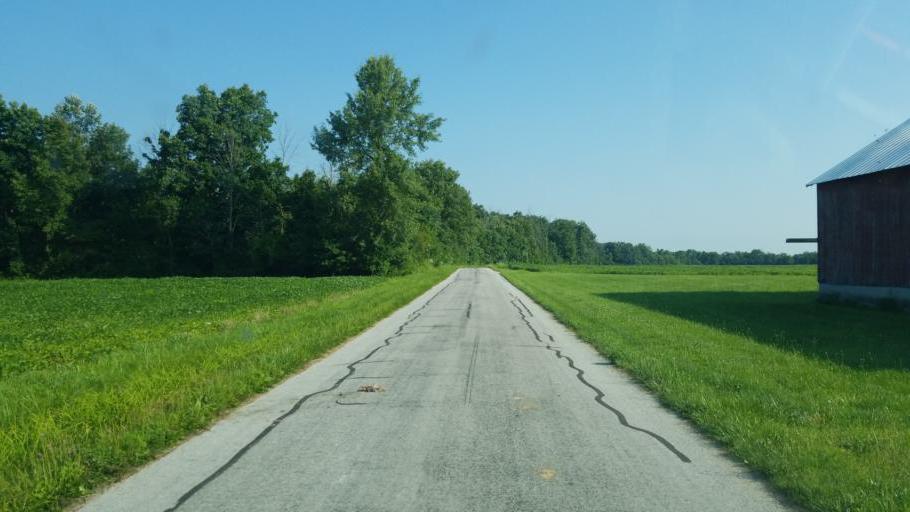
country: US
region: Ohio
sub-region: Hardin County
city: Kenton
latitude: 40.5991
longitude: -83.5416
